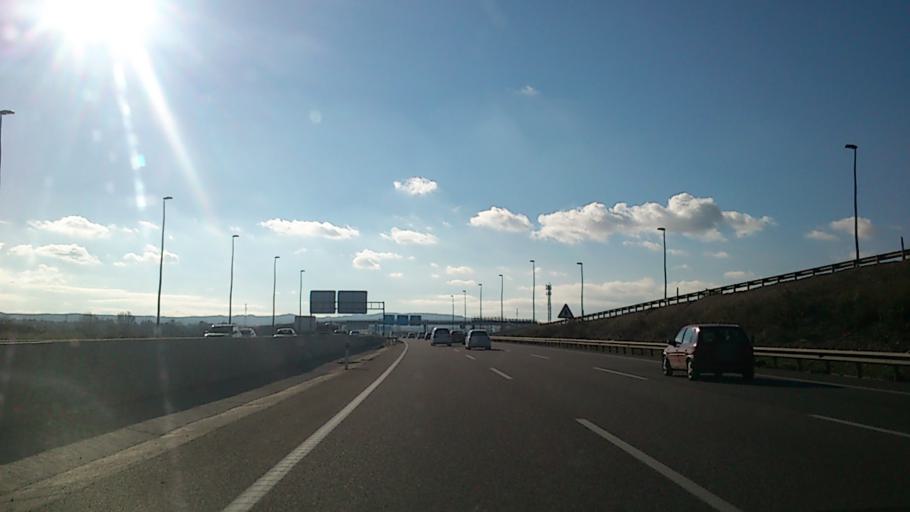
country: ES
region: Aragon
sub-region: Provincia de Zaragoza
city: Oliver-Valdefierro, Oliver, Valdefierro
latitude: 41.6564
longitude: -0.9549
